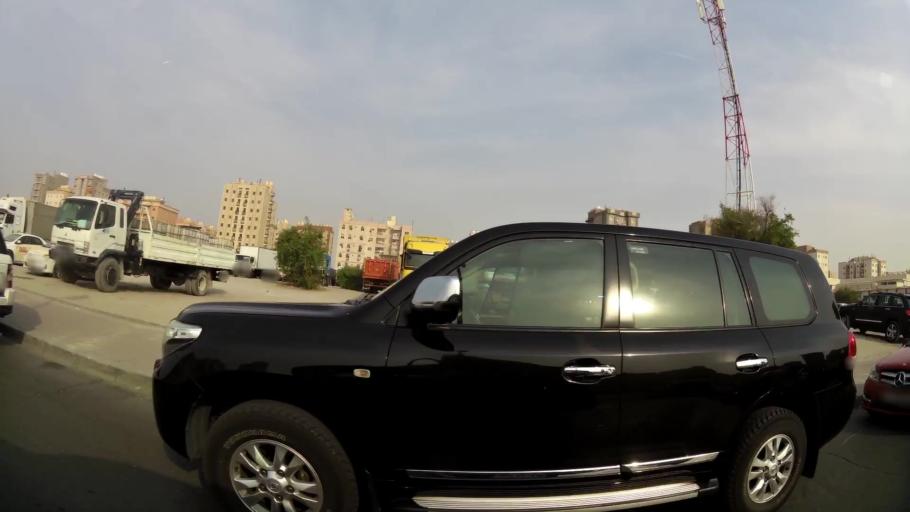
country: KW
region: Al Farwaniyah
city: Janub as Surrah
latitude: 29.2880
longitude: 47.9747
